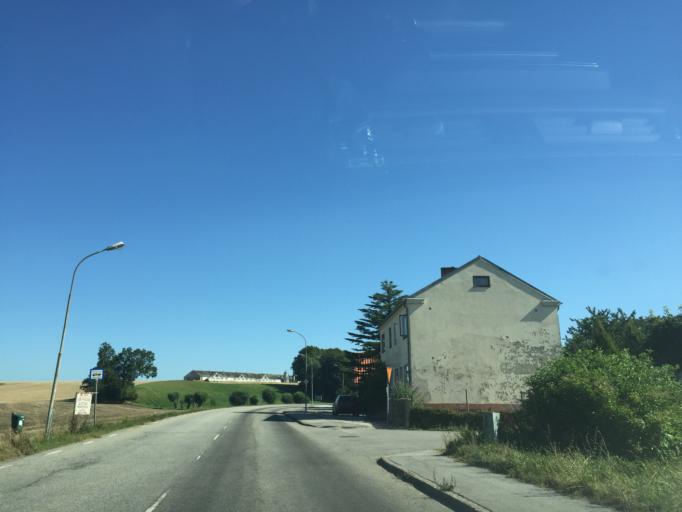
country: SE
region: Skane
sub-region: Ystads Kommun
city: Kopingebro
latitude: 55.4409
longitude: 14.1138
